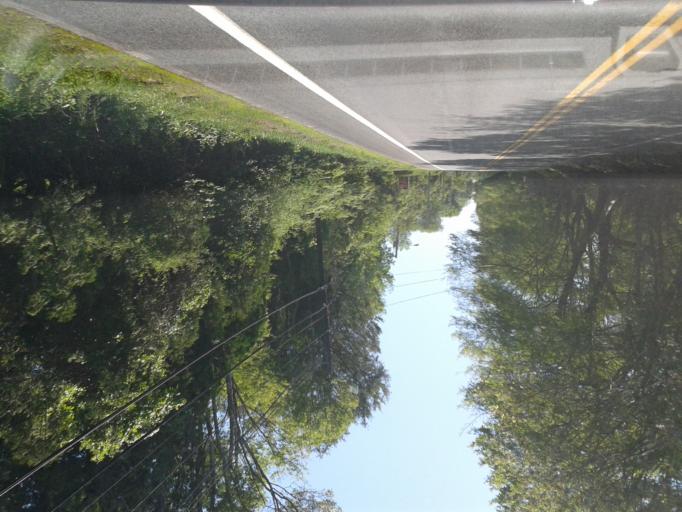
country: US
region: Rhode Island
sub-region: Washington County
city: Kingston
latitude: 41.4812
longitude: -71.5156
